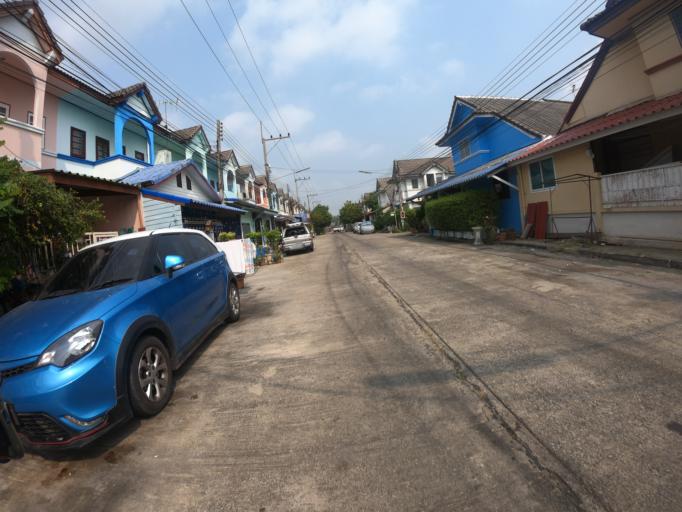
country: TH
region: Pathum Thani
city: Nong Suea
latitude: 14.0767
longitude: 100.8584
